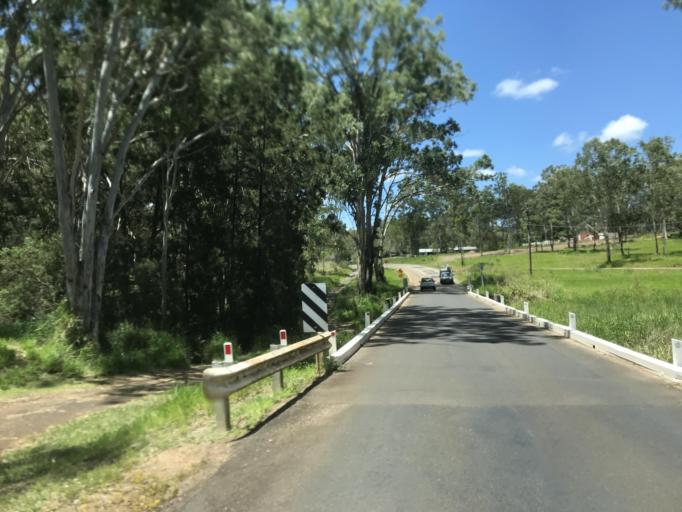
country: AU
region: Queensland
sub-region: Tablelands
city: Atherton
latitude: -17.4133
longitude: 145.3929
